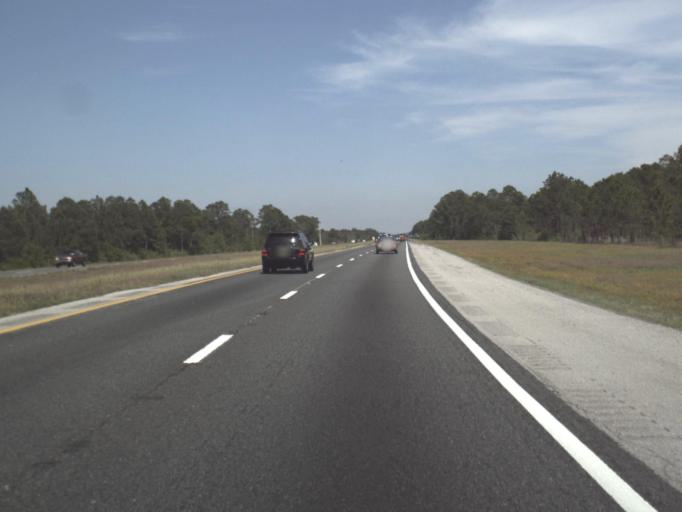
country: US
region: Florida
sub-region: Santa Rosa County
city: Pace
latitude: 30.5339
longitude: -87.1215
